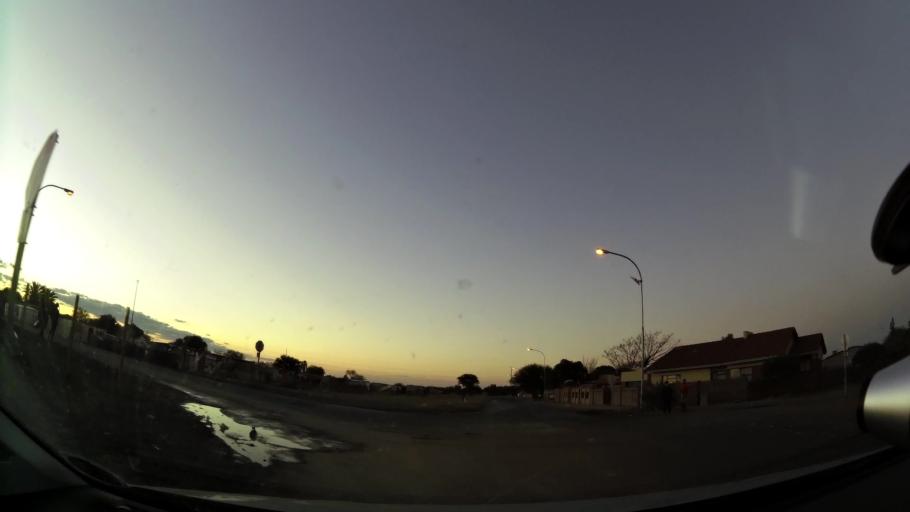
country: ZA
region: Northern Cape
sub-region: Frances Baard District Municipality
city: Kimberley
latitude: -28.7156
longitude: 24.7634
